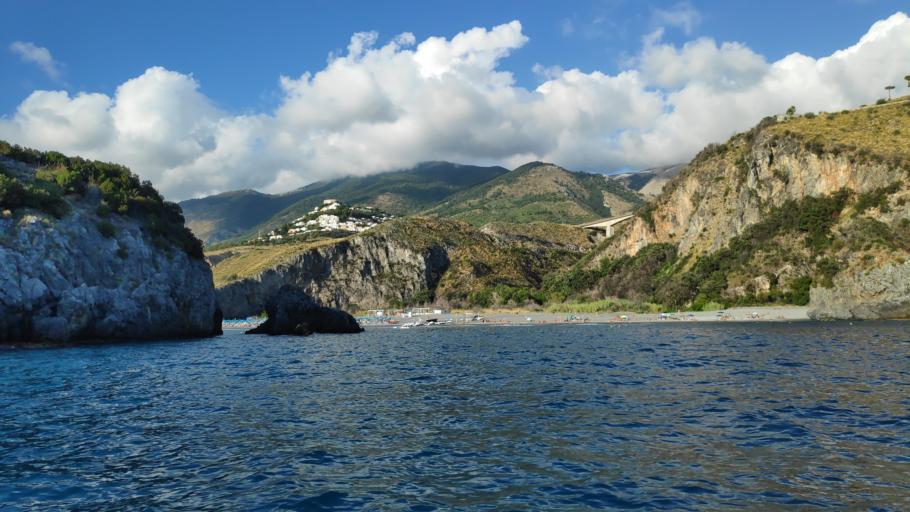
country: IT
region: Calabria
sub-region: Provincia di Cosenza
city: San Nicola Arcella
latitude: 39.8558
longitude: 15.7886
